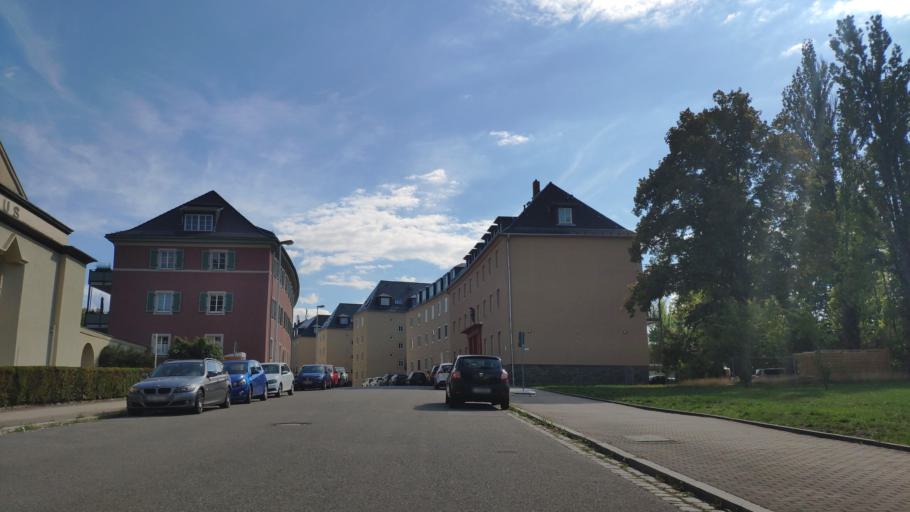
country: DE
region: Saxony
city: Chemnitz
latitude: 50.8300
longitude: 12.9352
